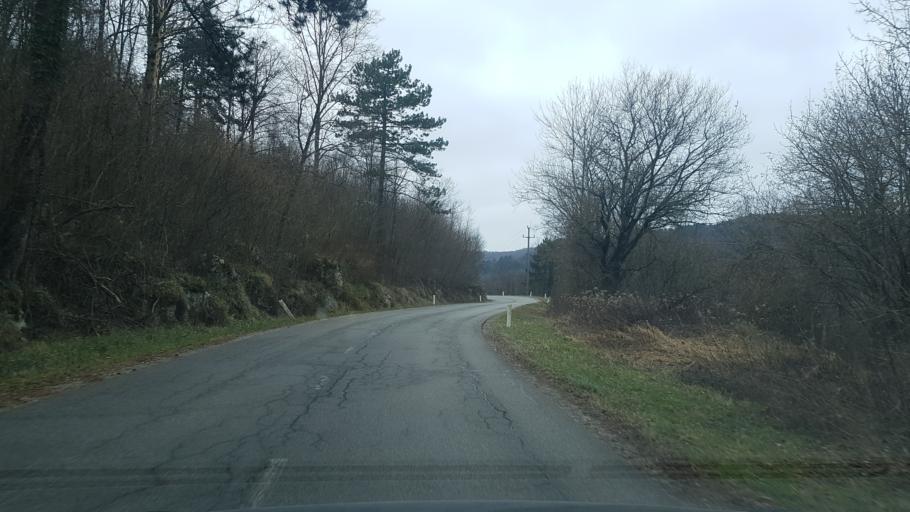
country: SI
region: Kanal
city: Kanal
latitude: 46.0434
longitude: 13.6734
